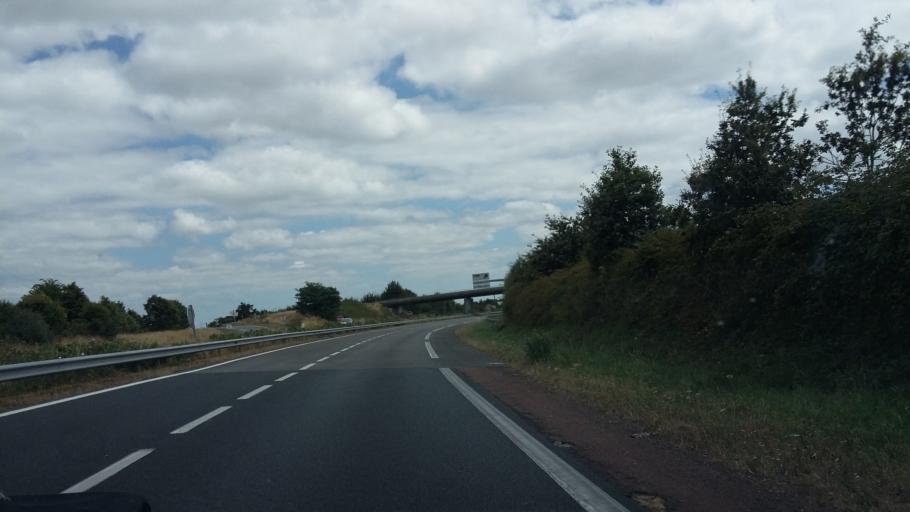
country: FR
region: Pays de la Loire
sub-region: Departement de la Vendee
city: Bournezeau
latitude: 46.6407
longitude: -1.1899
